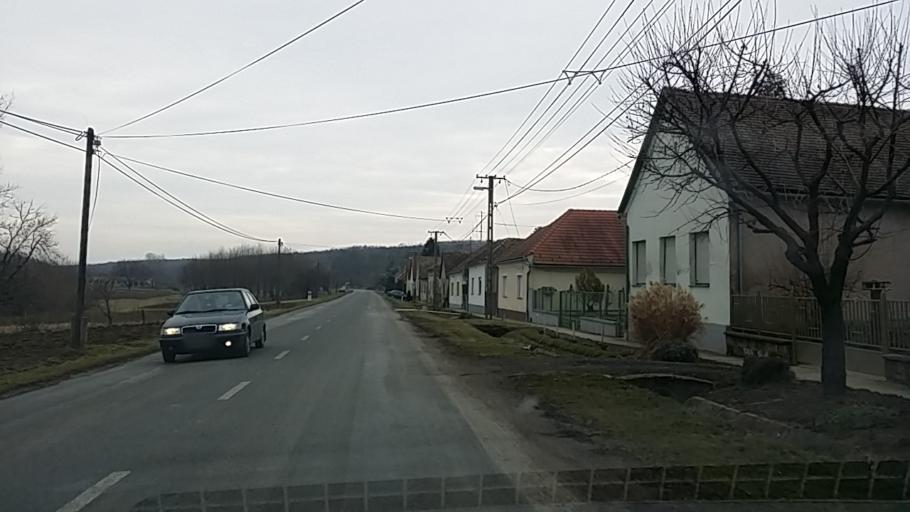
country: HU
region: Baranya
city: Lanycsok
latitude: 46.0436
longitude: 18.6047
